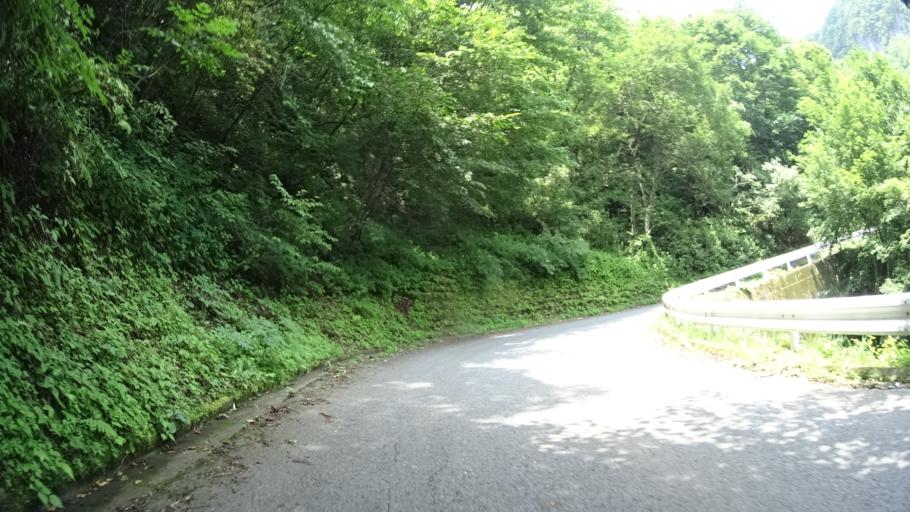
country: JP
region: Nagano
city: Saku
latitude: 36.0926
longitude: 138.6842
